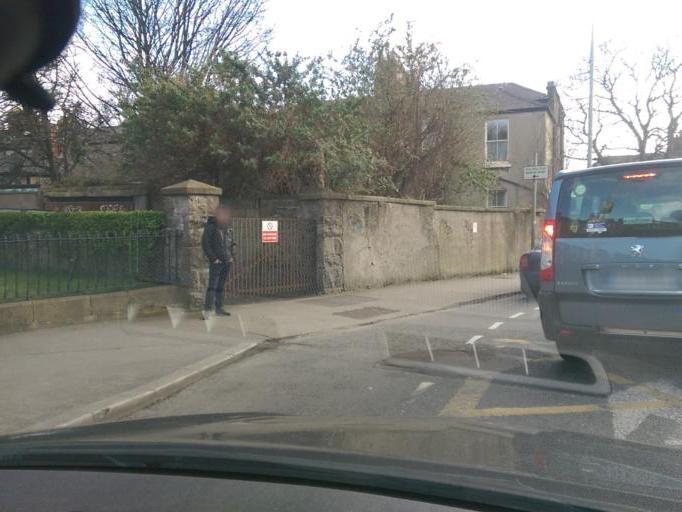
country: IE
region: Leinster
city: Drumcondra
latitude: 53.3639
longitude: -6.2574
